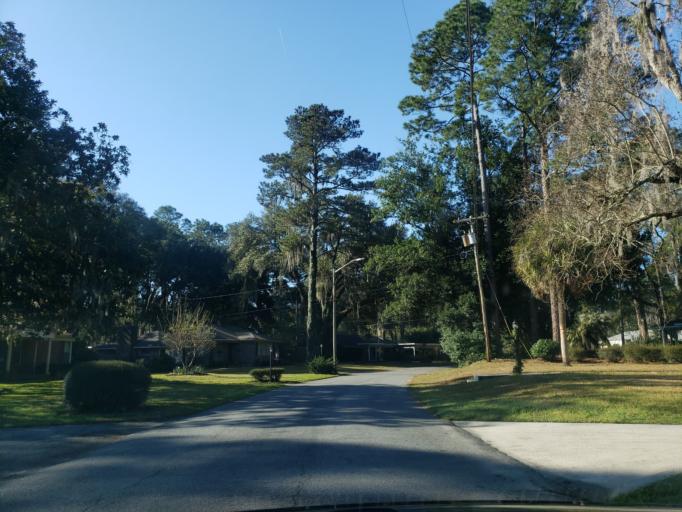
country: US
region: Georgia
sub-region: Chatham County
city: Thunderbolt
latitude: 32.0200
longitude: -81.0915
